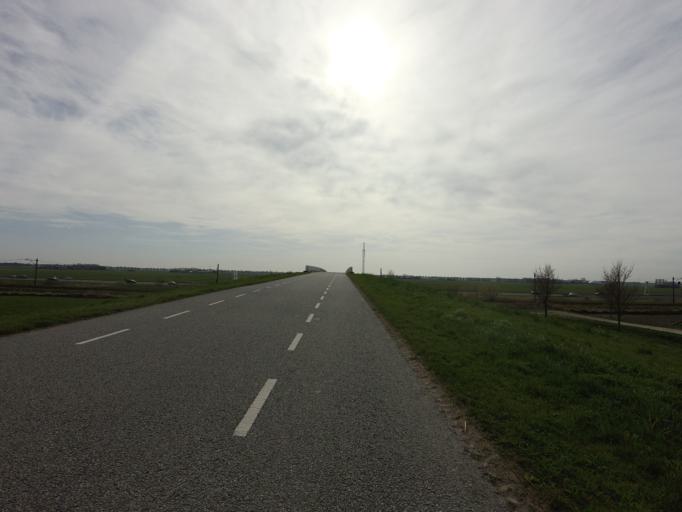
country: NL
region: South Holland
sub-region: Gemeente Alphen aan den Rijn
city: Alphen aan den Rijn
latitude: 52.1110
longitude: 4.6911
